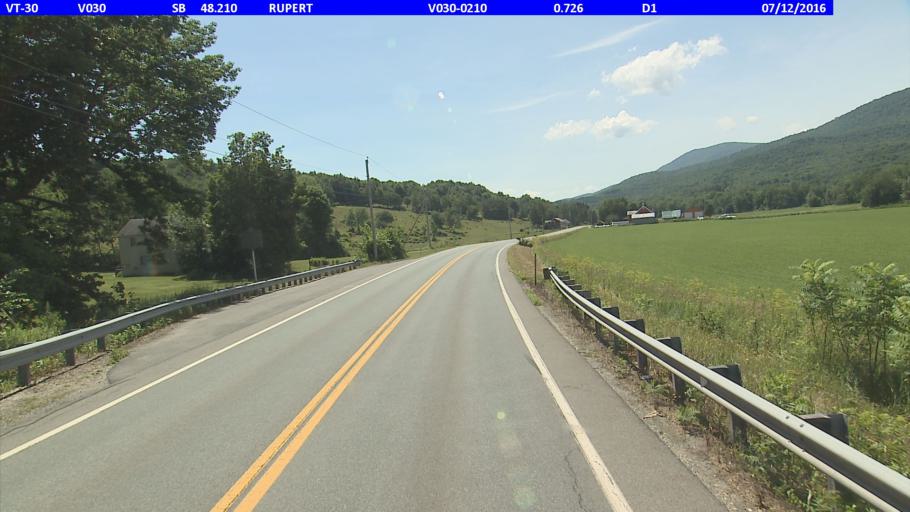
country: US
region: Vermont
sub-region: Bennington County
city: Manchester Center
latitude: 43.2810
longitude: -73.1260
